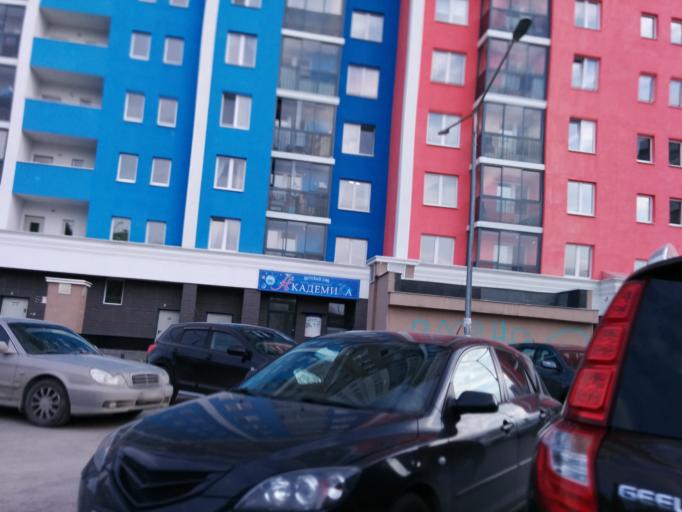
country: RU
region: Sverdlovsk
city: Shirokaya Rechka
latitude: 56.7952
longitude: 60.5173
